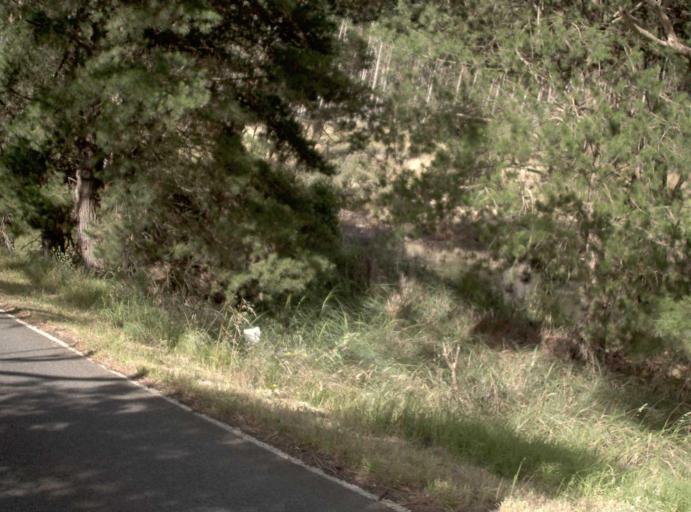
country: AU
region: Victoria
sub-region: Latrobe
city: Morwell
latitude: -38.1902
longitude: 146.4040
